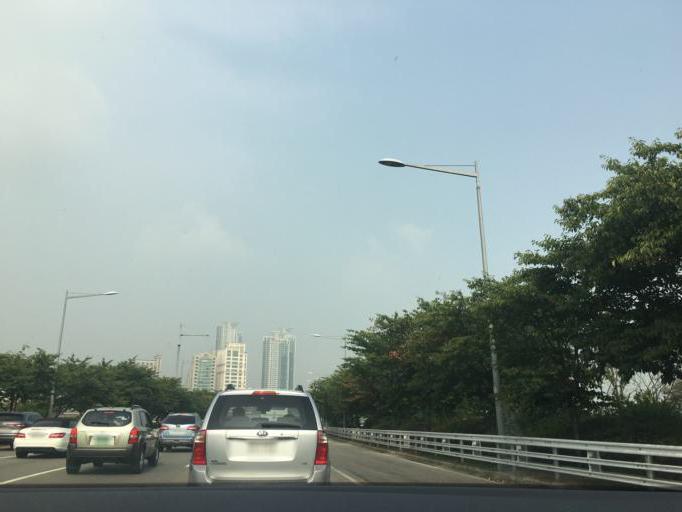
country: KR
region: Gyeonggi-do
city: Seongnam-si
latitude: 37.5185
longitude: 127.0713
